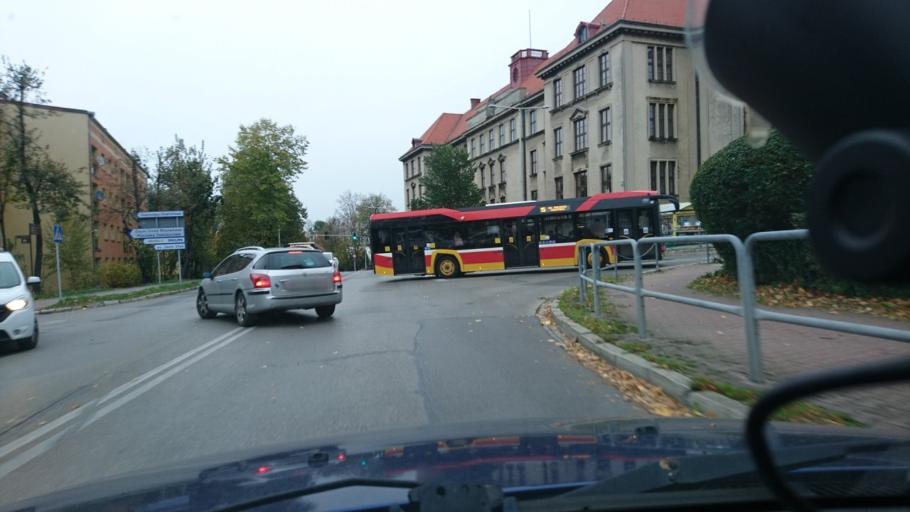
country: PL
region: Silesian Voivodeship
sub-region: Bielsko-Biala
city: Bielsko-Biala
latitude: 49.8265
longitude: 19.0341
